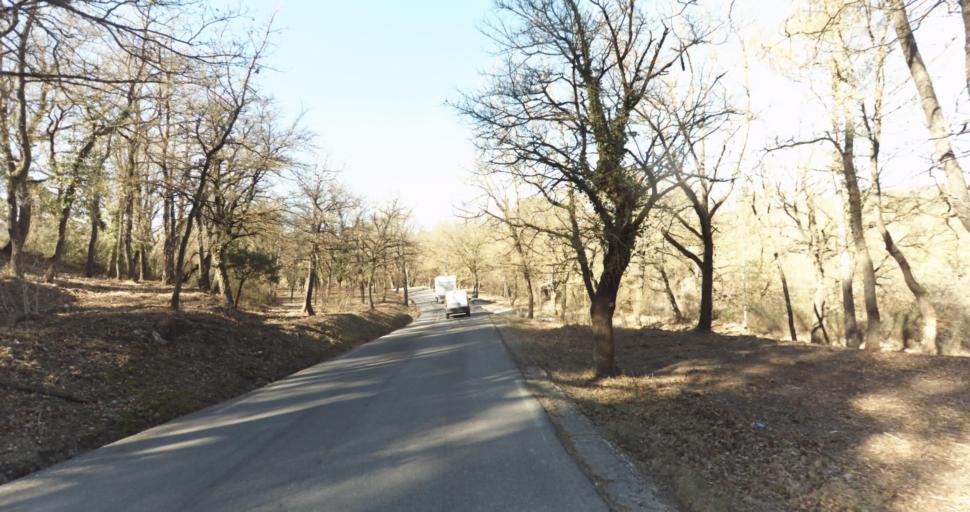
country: FR
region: Provence-Alpes-Cote d'Azur
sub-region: Departement des Bouches-du-Rhone
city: Peypin
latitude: 43.3942
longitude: 5.5678
